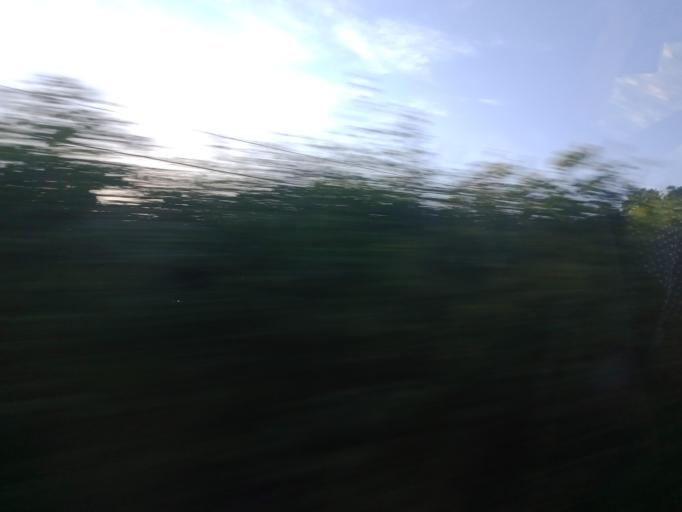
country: IE
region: Leinster
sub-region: Kilkenny
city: Kilkenny
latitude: 52.7240
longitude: -7.2374
